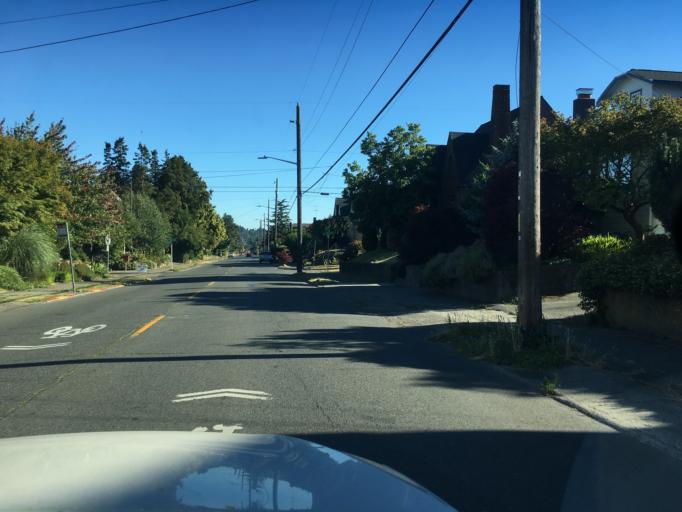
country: US
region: Washington
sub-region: King County
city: Shoreline
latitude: 47.6808
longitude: -122.3984
